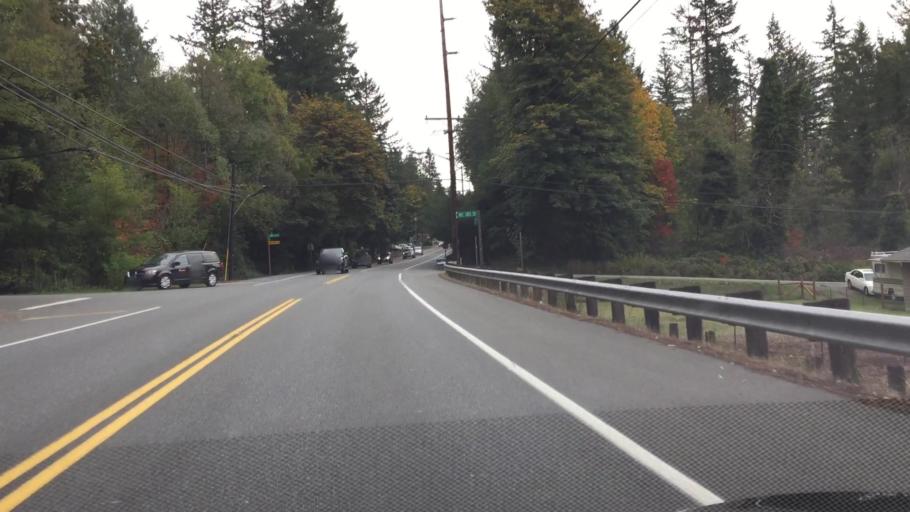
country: US
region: Washington
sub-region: King County
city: Cottage Lake
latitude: 47.7598
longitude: -122.0918
